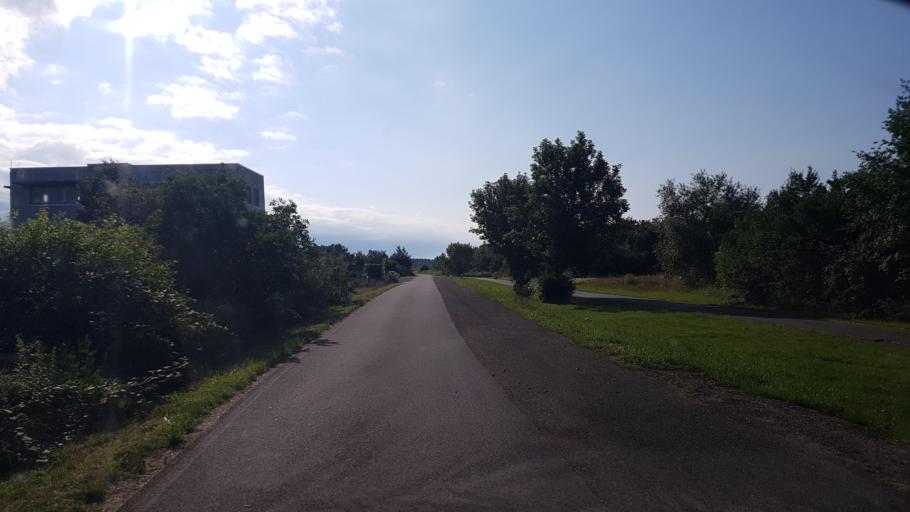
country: DE
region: Brandenburg
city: Grossraschen
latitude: 51.5760
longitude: 14.0240
